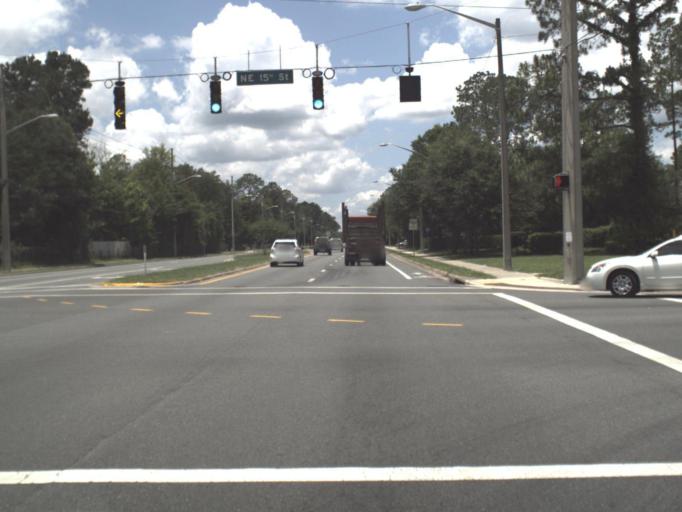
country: US
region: Florida
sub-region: Alachua County
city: Gainesville
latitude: 29.6884
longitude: -82.3056
